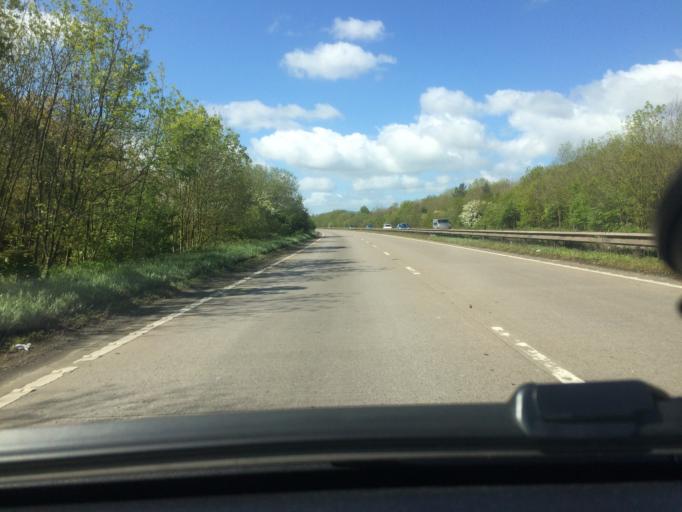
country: GB
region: Wales
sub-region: Wrexham
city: Rossett
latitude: 53.1458
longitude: -2.9316
